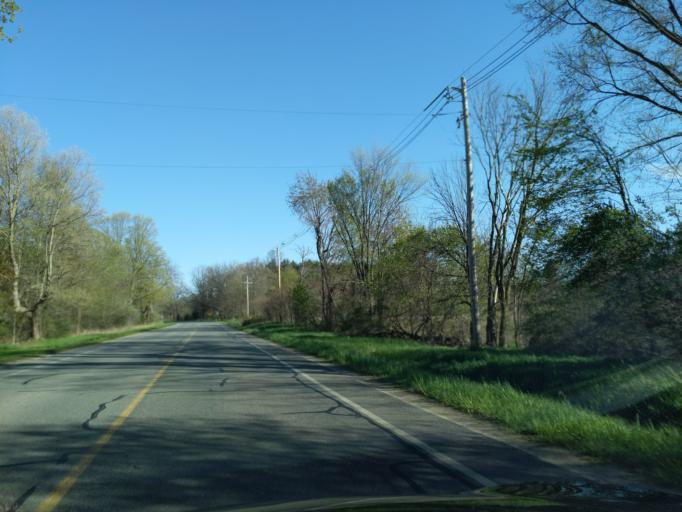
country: US
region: Michigan
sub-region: Ionia County
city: Portland
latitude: 42.8516
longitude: -84.8779
